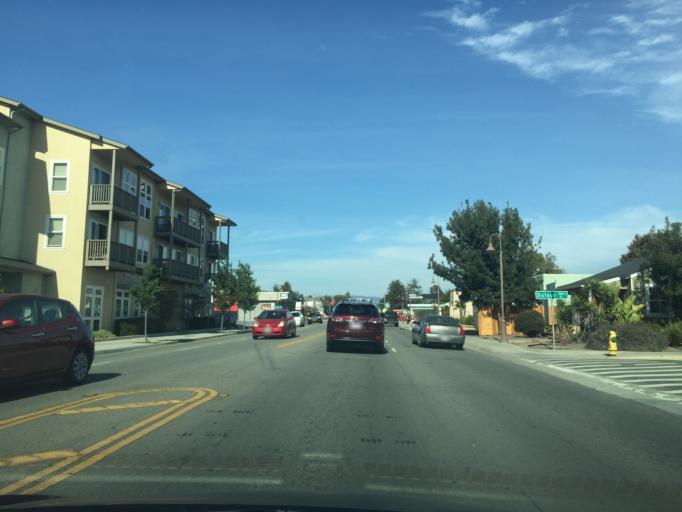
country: US
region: California
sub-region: Santa Cruz County
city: Santa Cruz
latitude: 36.9638
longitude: -122.0428
